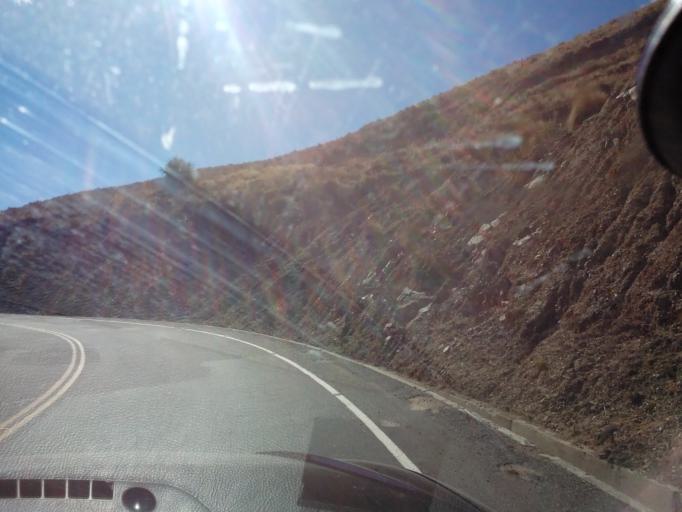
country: PE
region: Apurimac
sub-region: Provincia de Abancay
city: Tamburco
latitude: -13.5860
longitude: -72.8195
